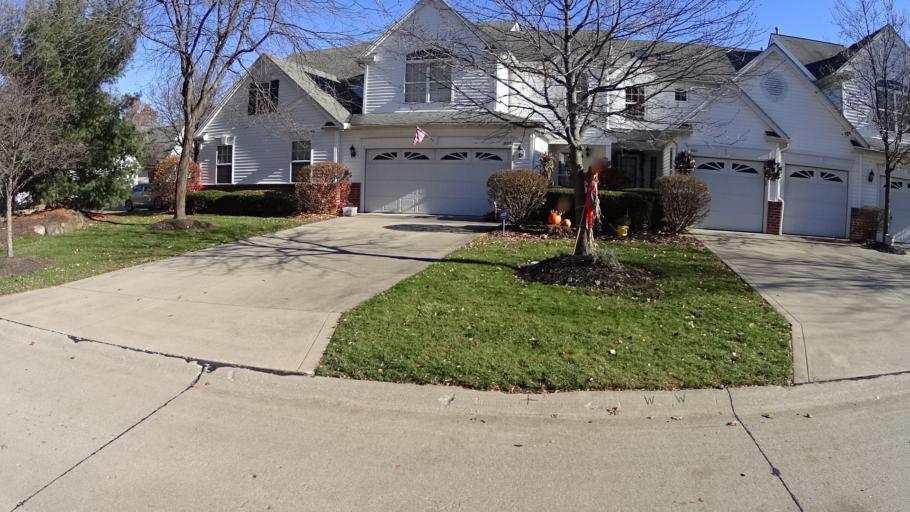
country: US
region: Ohio
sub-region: Lorain County
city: Avon Center
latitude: 41.4635
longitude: -82.0290
